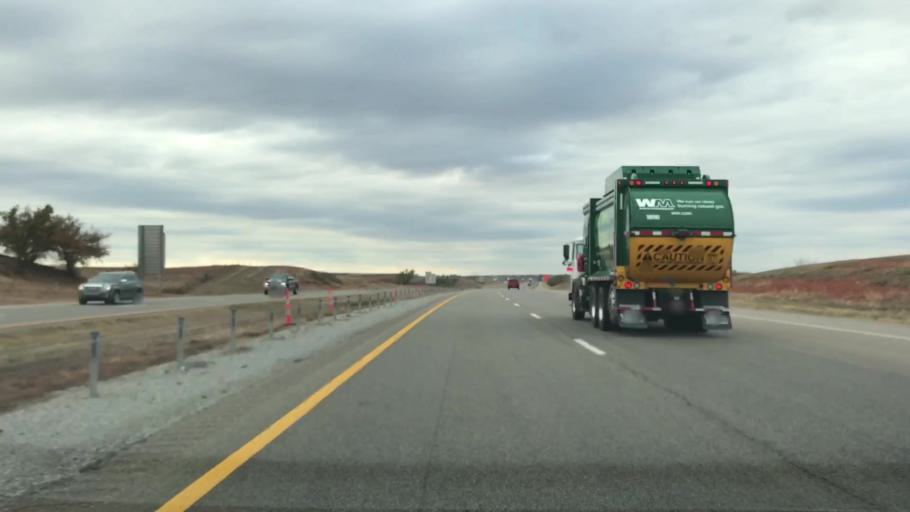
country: US
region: Oklahoma
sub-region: Washita County
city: Burns Flat
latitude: 35.4422
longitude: -99.1758
